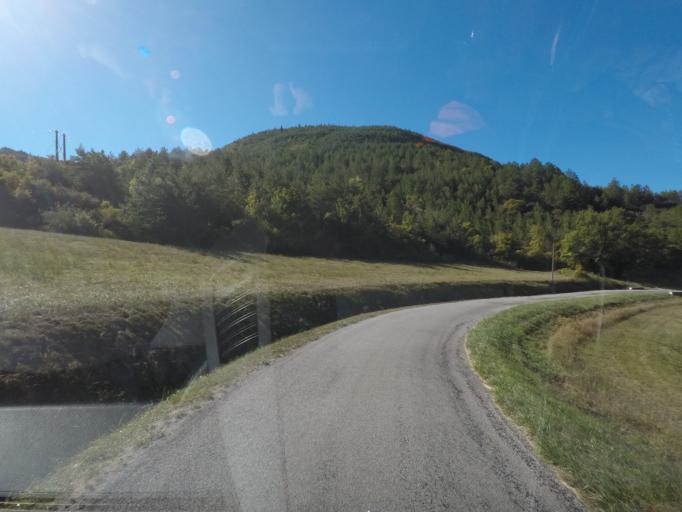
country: FR
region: Rhone-Alpes
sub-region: Departement de la Drome
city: Die
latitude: 44.5608
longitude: 5.3391
